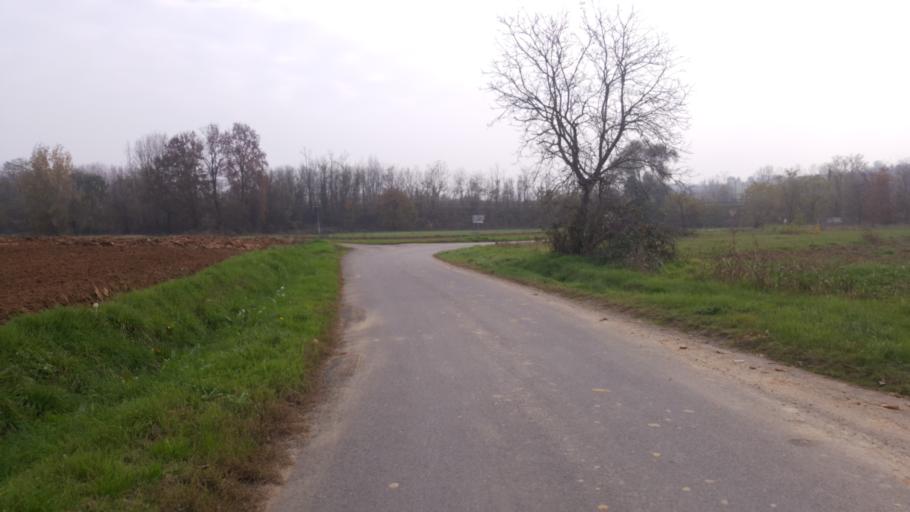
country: IT
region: Piedmont
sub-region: Provincia di Asti
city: Cerro Tanaro
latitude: 44.9062
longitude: 8.3682
